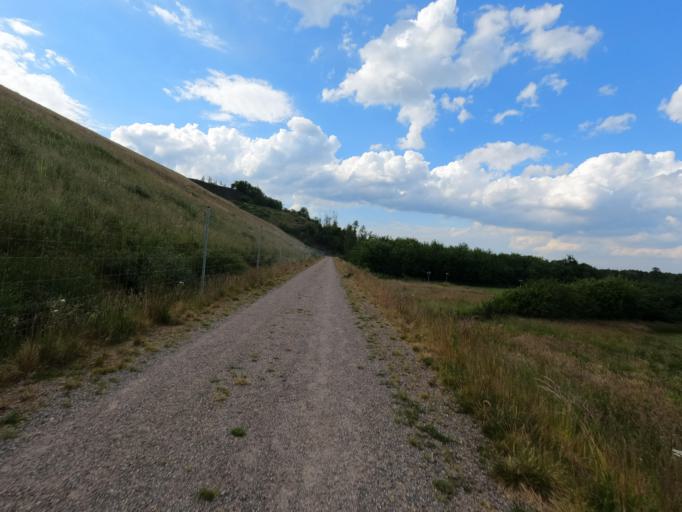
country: DE
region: North Rhine-Westphalia
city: Huckelhoven
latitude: 51.0803
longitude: 6.2038
